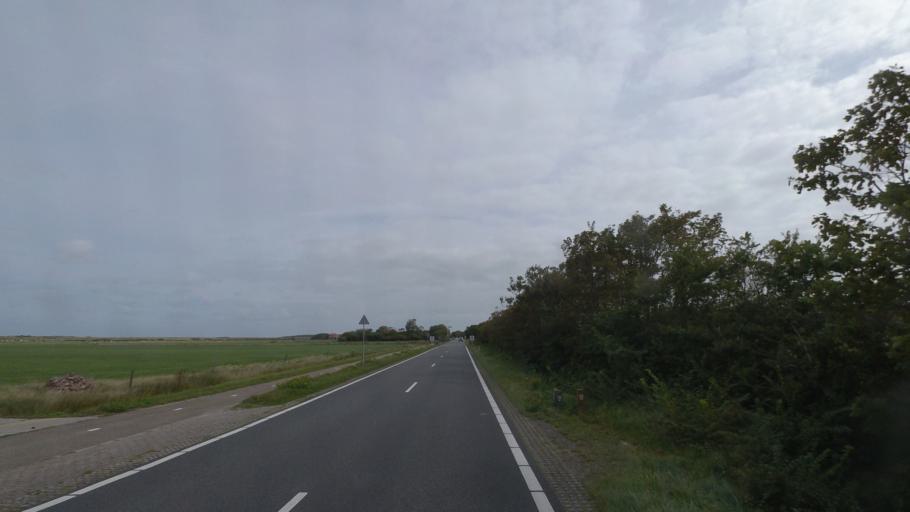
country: NL
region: Friesland
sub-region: Gemeente Ameland
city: Nes
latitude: 53.4454
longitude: 5.7181
